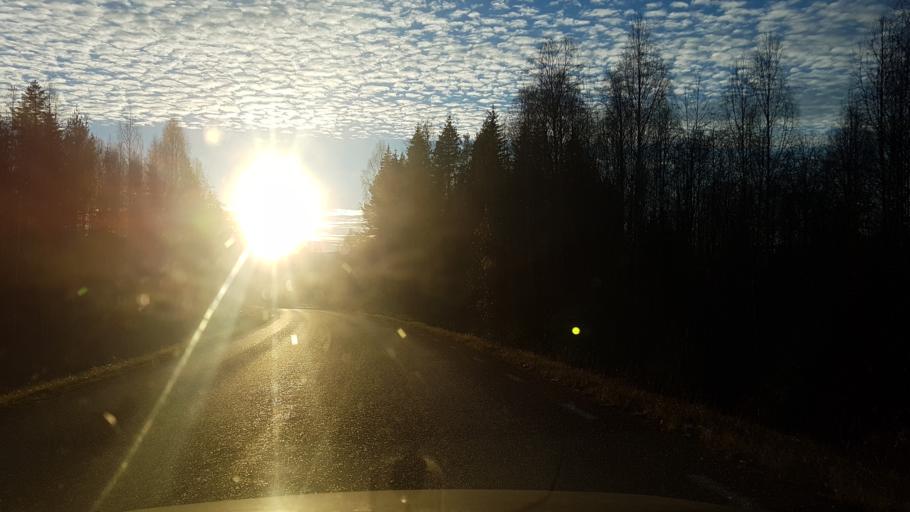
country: SE
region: Dalarna
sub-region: Leksand Municipality
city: Smedby
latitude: 60.7175
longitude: 15.0999
